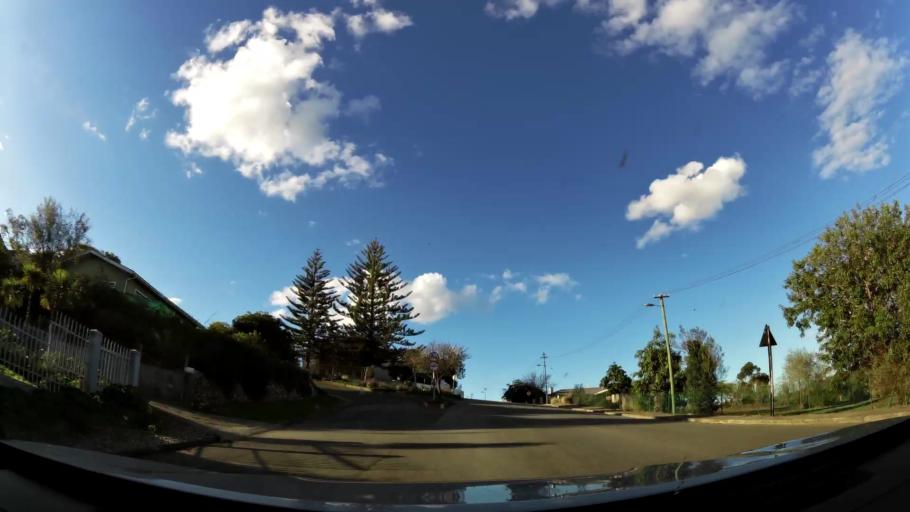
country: ZA
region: Western Cape
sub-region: Eden District Municipality
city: Riversdale
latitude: -34.0876
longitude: 20.9589
